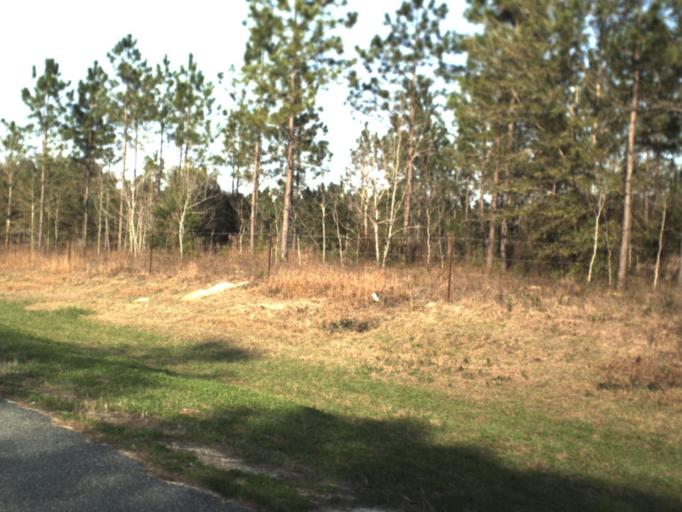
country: US
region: Florida
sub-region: Calhoun County
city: Blountstown
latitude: 30.5275
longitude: -85.1933
